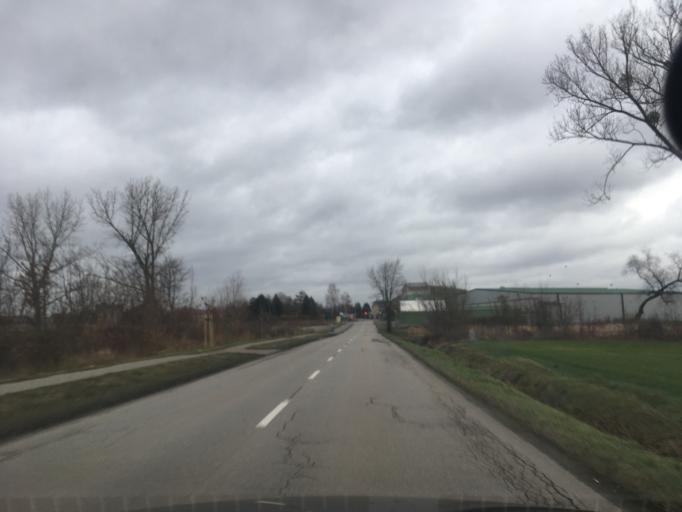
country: PL
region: Masovian Voivodeship
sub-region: Powiat pruszkowski
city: Rybie
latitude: 52.1330
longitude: 20.9725
